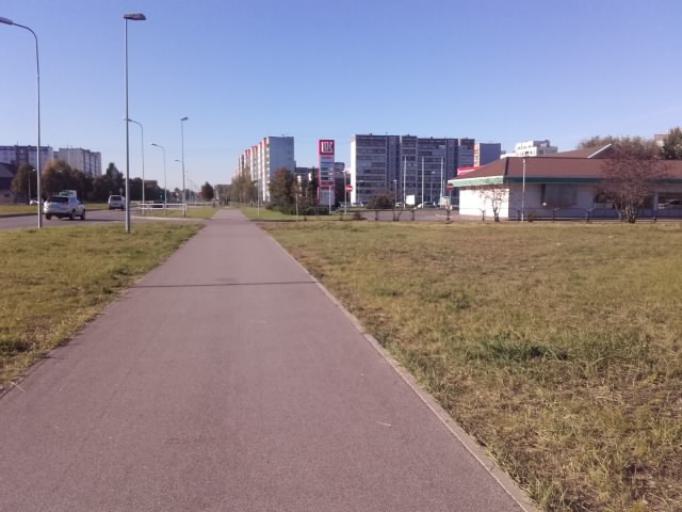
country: LV
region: Stopini
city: Ulbroka
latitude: 56.9379
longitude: 24.2169
